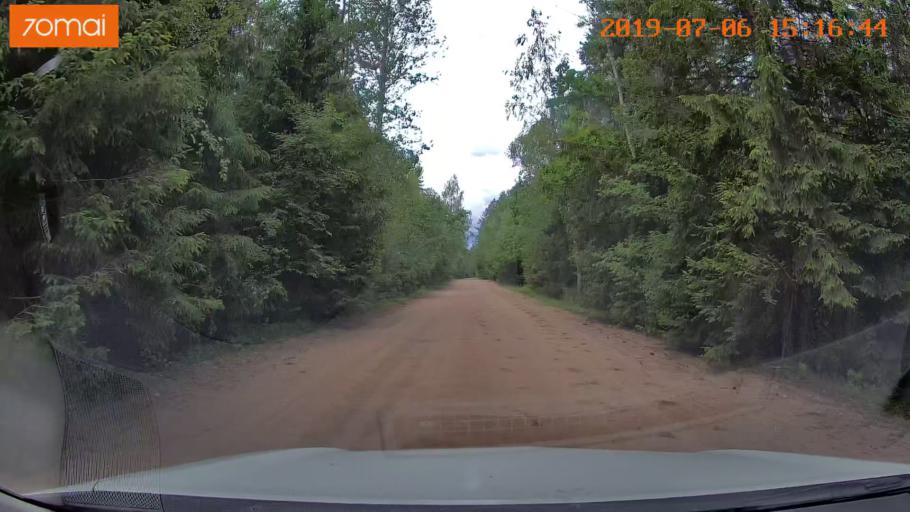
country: BY
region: Minsk
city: Ivyanyets
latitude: 53.9832
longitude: 26.6749
